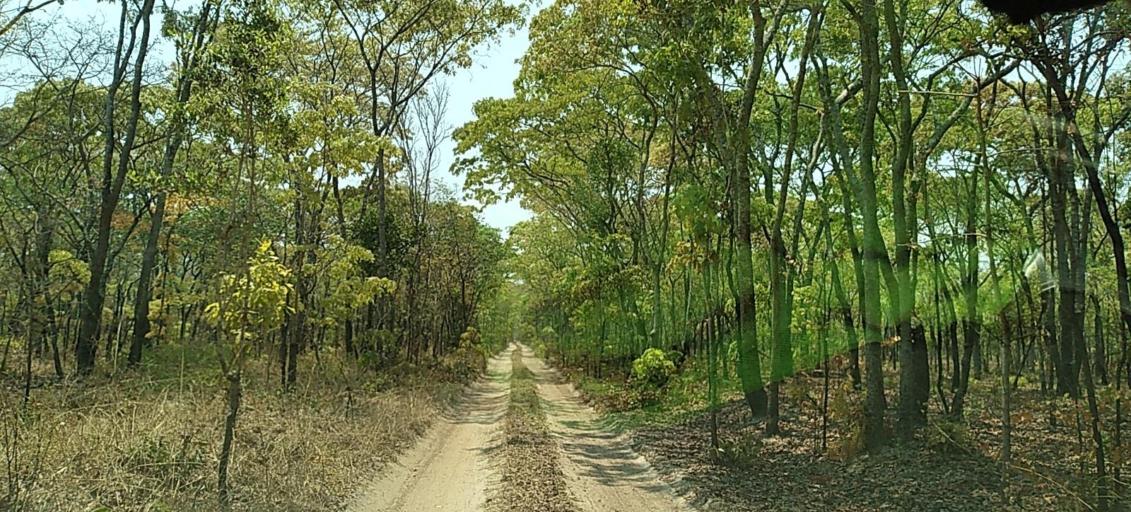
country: ZM
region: North-Western
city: Kabompo
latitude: -13.6523
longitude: 24.4709
